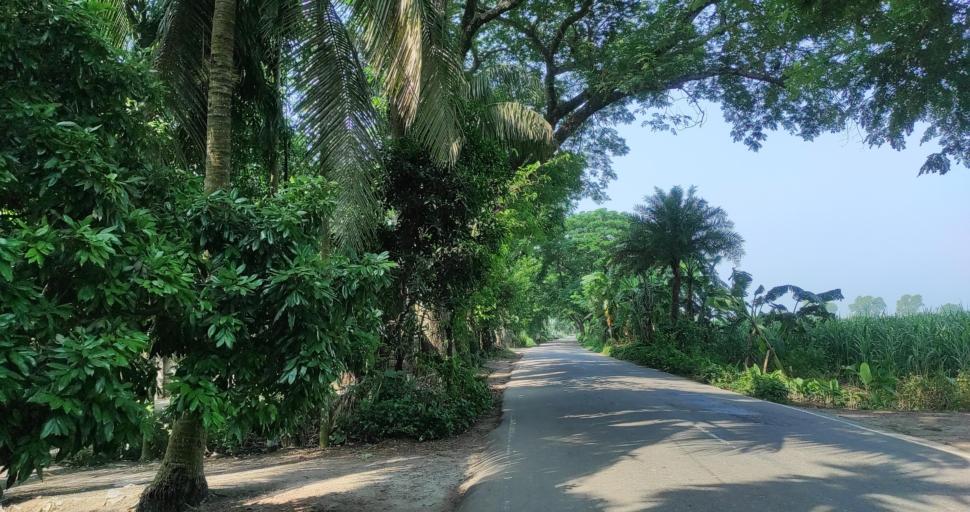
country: BD
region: Rajshahi
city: Ishurdi
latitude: 24.2728
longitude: 89.0560
